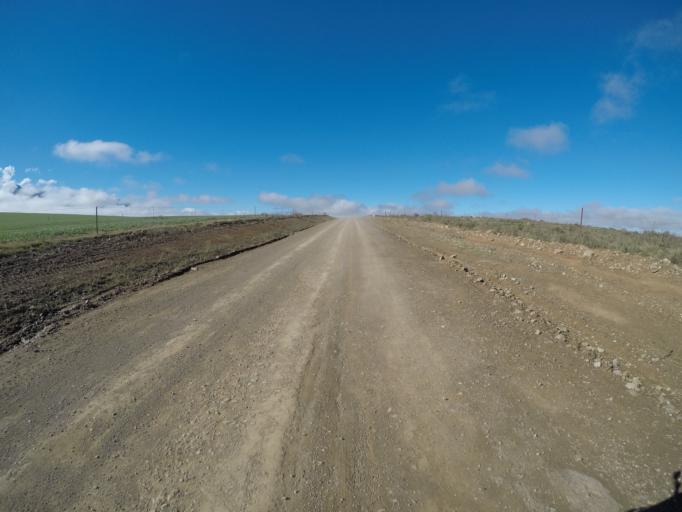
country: ZA
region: Western Cape
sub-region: Overberg District Municipality
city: Caledon
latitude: -34.1197
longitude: 19.7201
